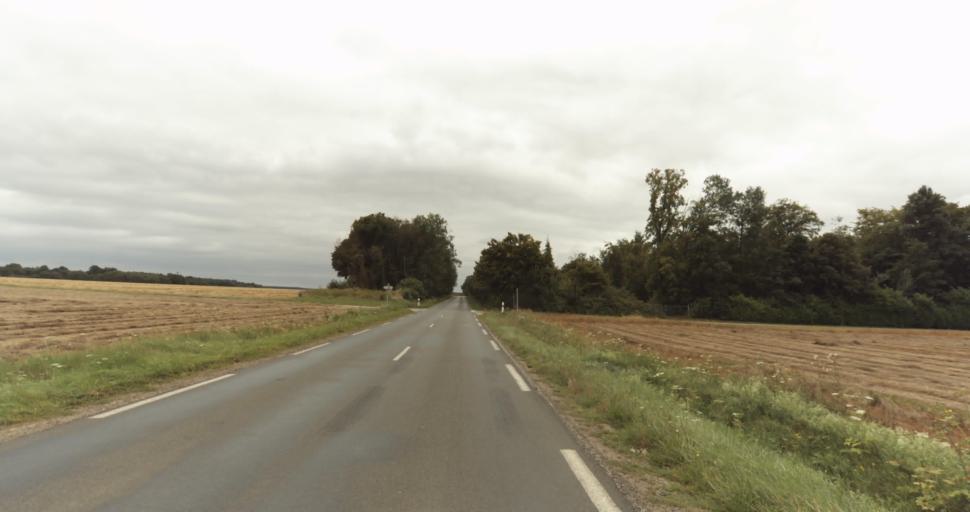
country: FR
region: Haute-Normandie
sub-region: Departement de l'Eure
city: Gravigny
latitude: 49.0203
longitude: 1.2427
